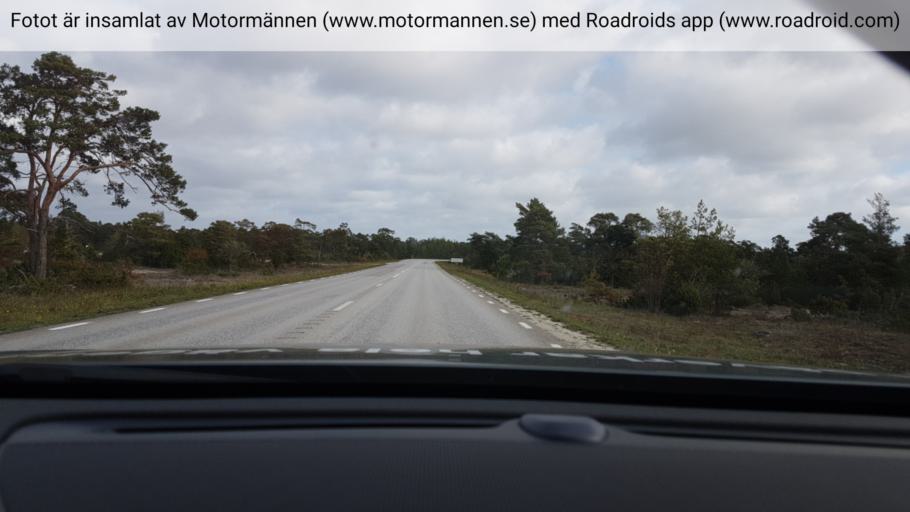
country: SE
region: Gotland
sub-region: Gotland
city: Slite
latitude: 57.8449
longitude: 18.9648
